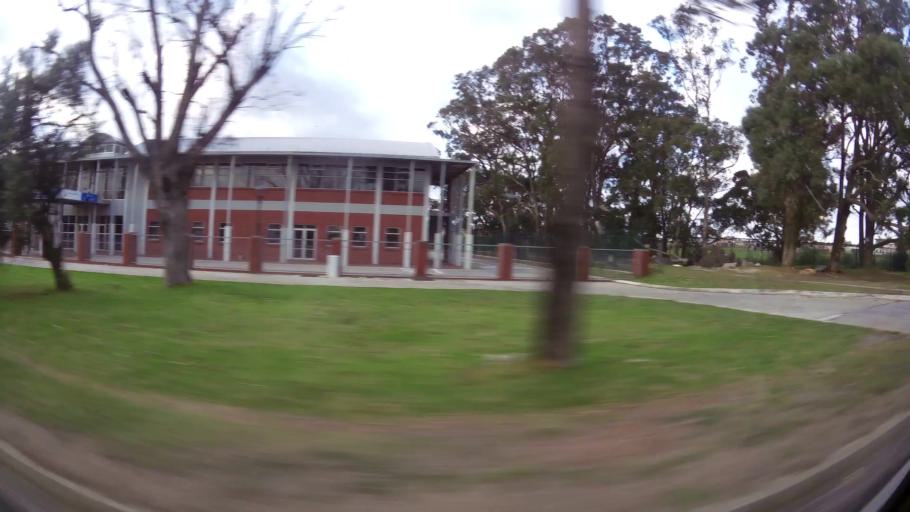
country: ZA
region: Eastern Cape
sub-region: Nelson Mandela Bay Metropolitan Municipality
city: Port Elizabeth
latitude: -33.9832
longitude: 25.5896
